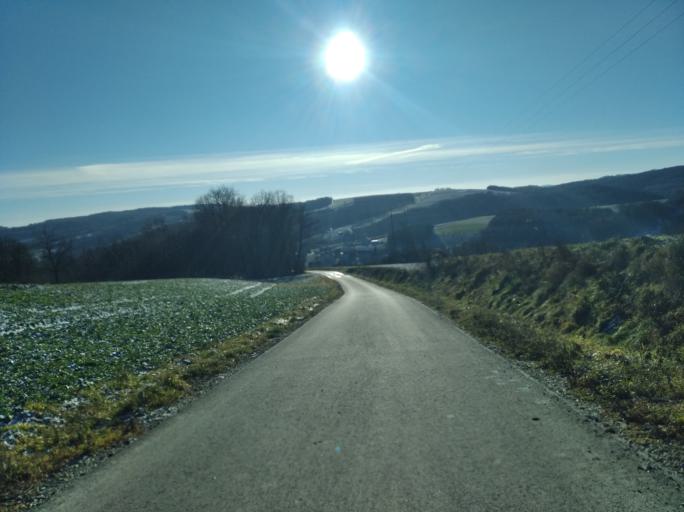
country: PL
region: Subcarpathian Voivodeship
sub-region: Powiat strzyzowski
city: Strzyzow
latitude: 49.9367
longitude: 21.7688
